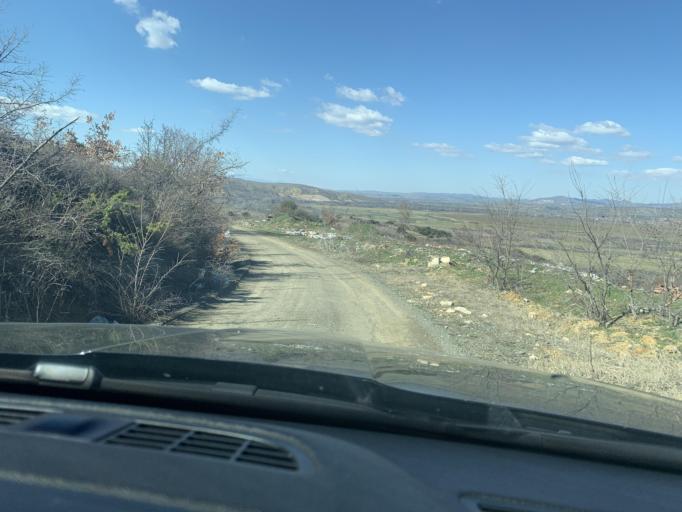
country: MK
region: Demir Kapija
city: Demir Kapija
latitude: 41.4141
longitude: 22.2142
